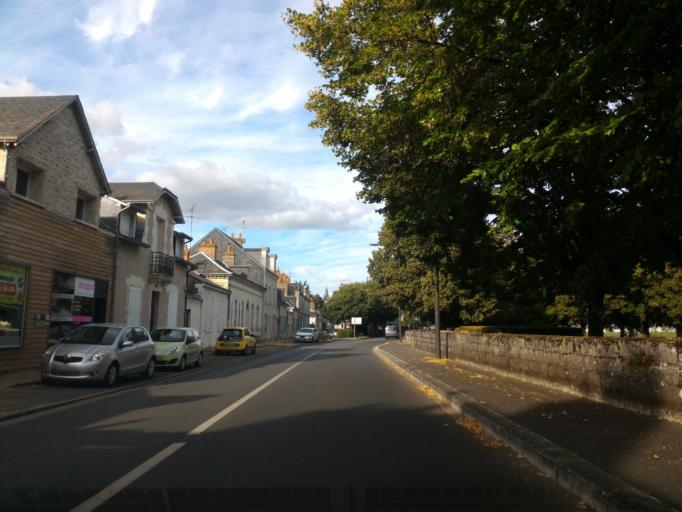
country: FR
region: Centre
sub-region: Departement du Loir-et-Cher
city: Blois
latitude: 47.5787
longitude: 1.3221
